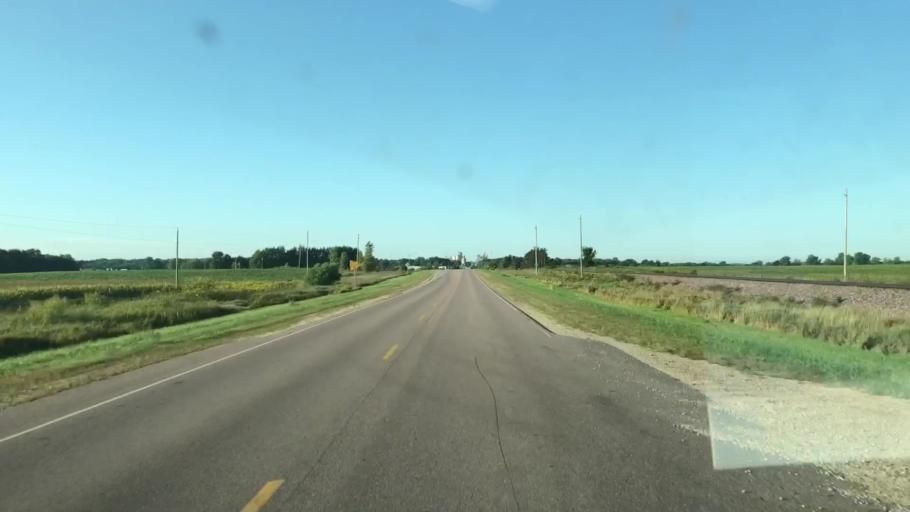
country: US
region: Iowa
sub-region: O'Brien County
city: Sheldon
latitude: 43.2093
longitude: -95.8417
